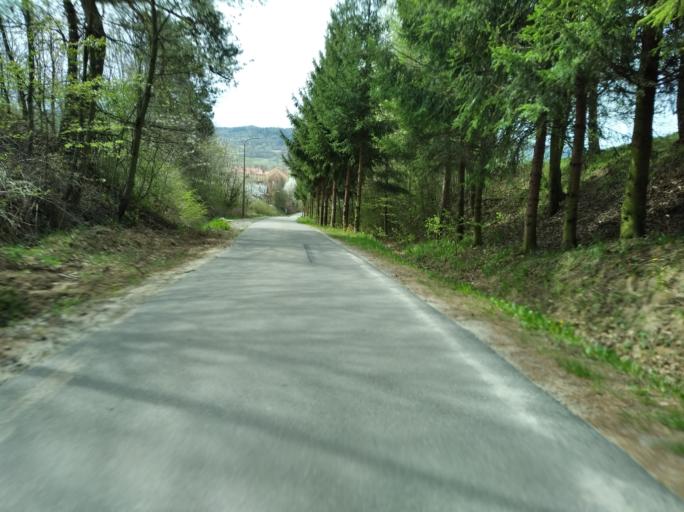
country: PL
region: Subcarpathian Voivodeship
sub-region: Powiat strzyzowski
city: Wisniowa
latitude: 49.8768
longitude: 21.6688
